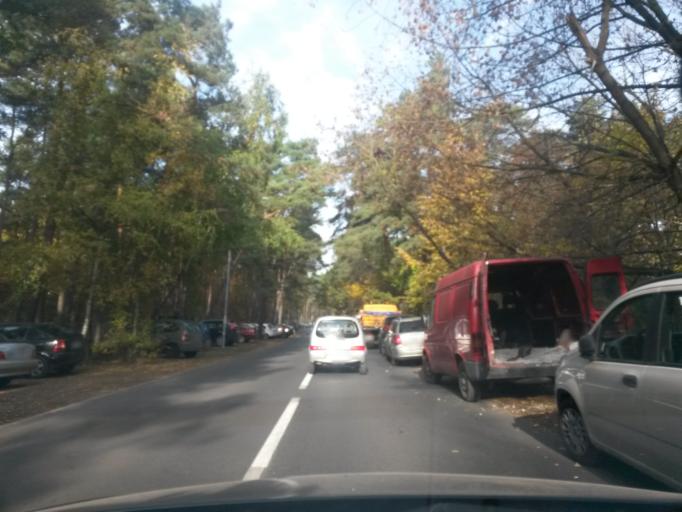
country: PL
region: Greater Poland Voivodeship
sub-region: Powiat poznanski
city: Plewiska
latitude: 52.3930
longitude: 16.8247
